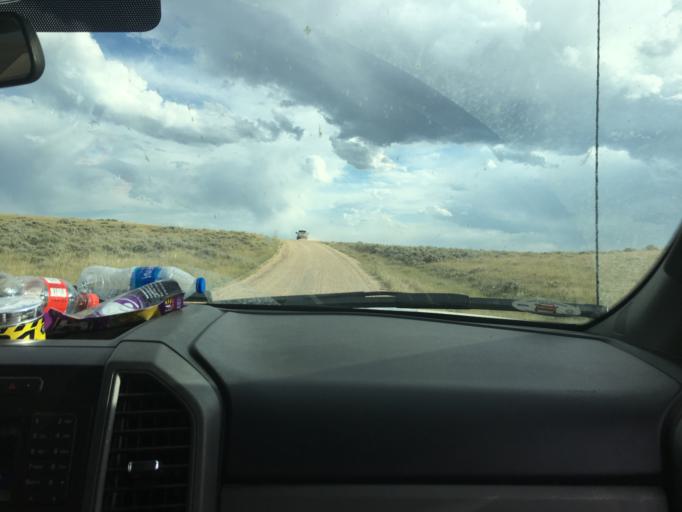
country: US
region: Wyoming
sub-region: Campbell County
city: Wright
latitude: 43.4928
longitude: -105.8592
